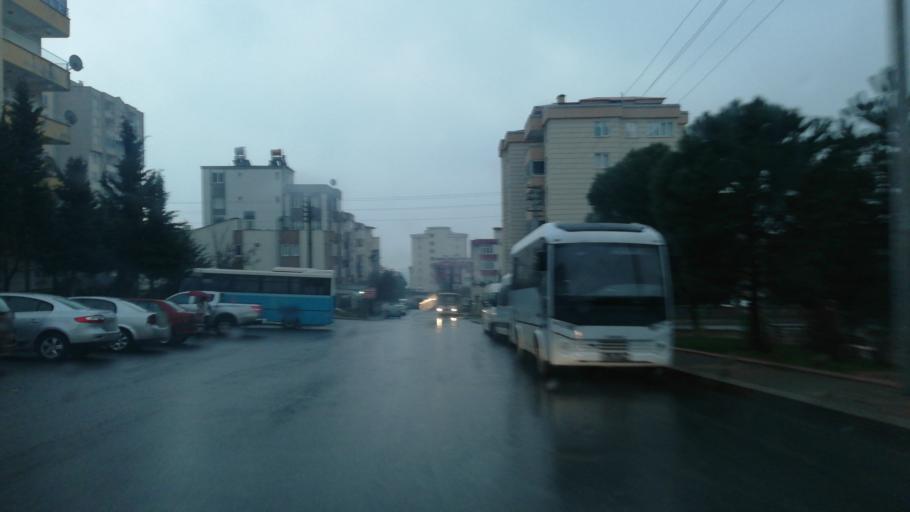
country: TR
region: Kahramanmaras
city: Kahramanmaras
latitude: 37.5956
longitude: 36.8994
